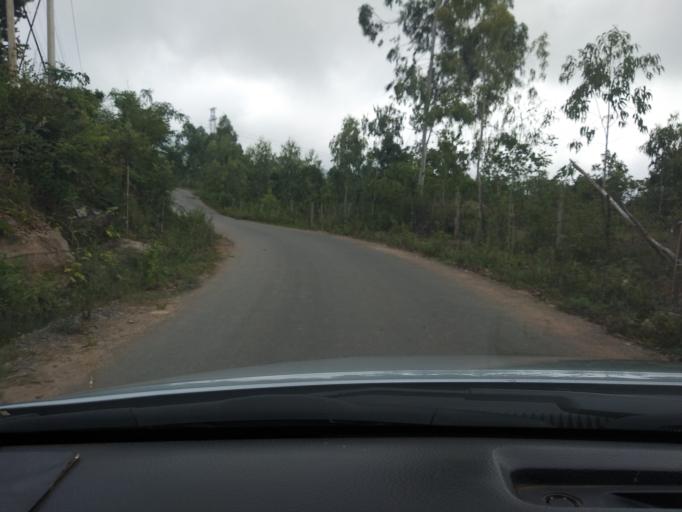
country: MM
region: Mandalay
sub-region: Pyin Oo Lwin District
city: Pyin Oo Lwin
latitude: 21.9133
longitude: 96.3826
